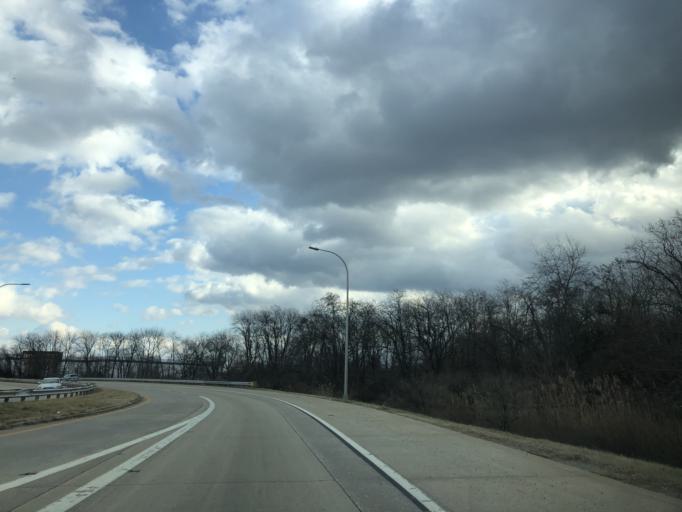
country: US
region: Delaware
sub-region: New Castle County
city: Wilmington
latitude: 39.7149
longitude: -75.5579
